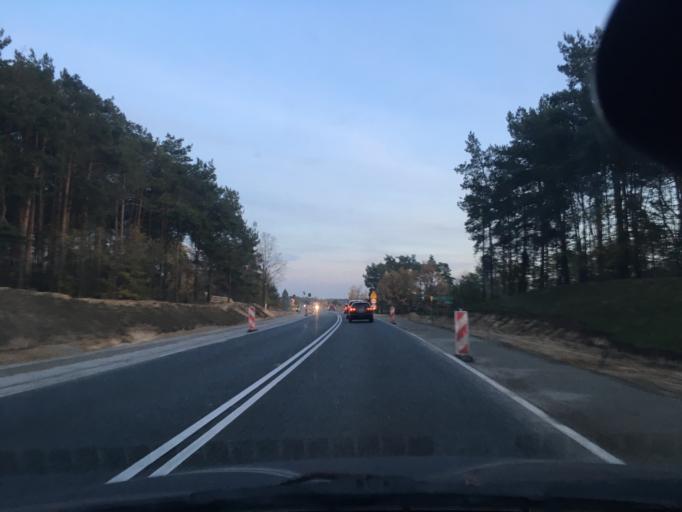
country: PL
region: Masovian Voivodeship
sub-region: Powiat plocki
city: Wyszogrod
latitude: 52.3624
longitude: 20.1970
